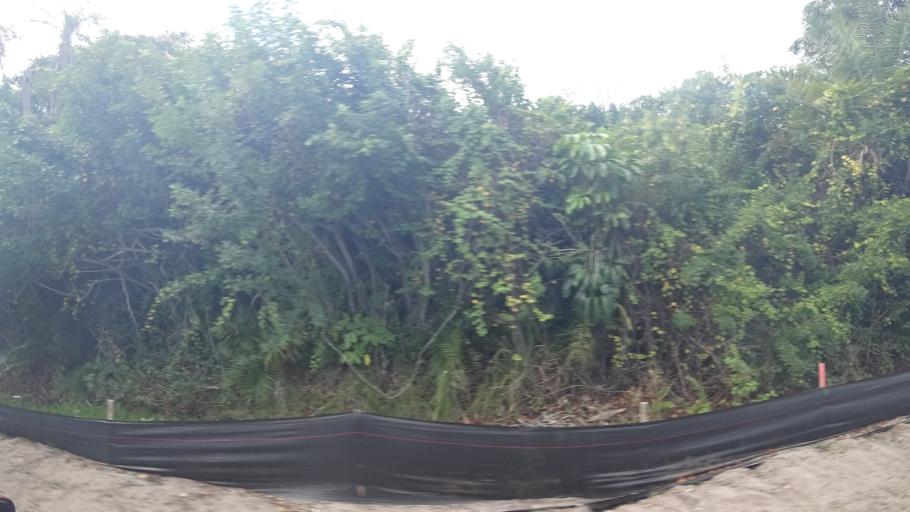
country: US
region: Florida
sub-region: Manatee County
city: West Bradenton
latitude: 27.5128
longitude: -82.6610
